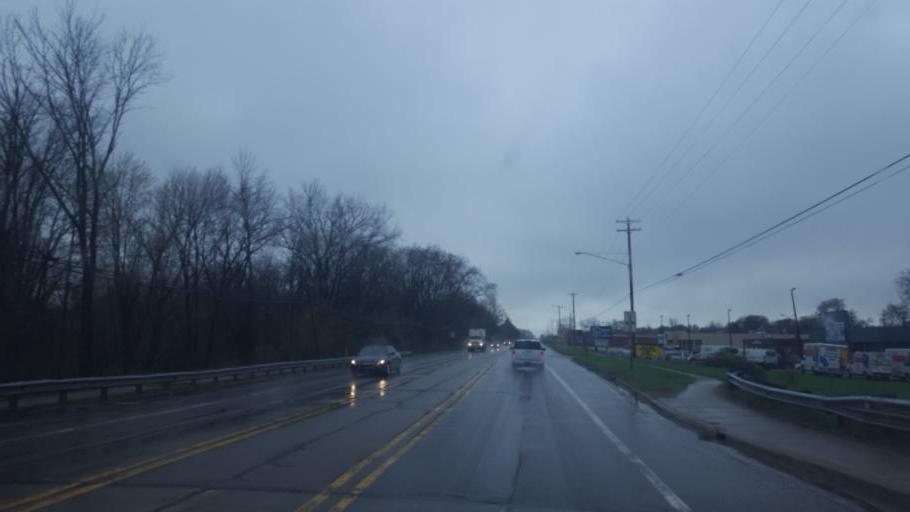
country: US
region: Michigan
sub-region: Isabella County
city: Mount Pleasant
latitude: 43.5971
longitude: -84.7866
